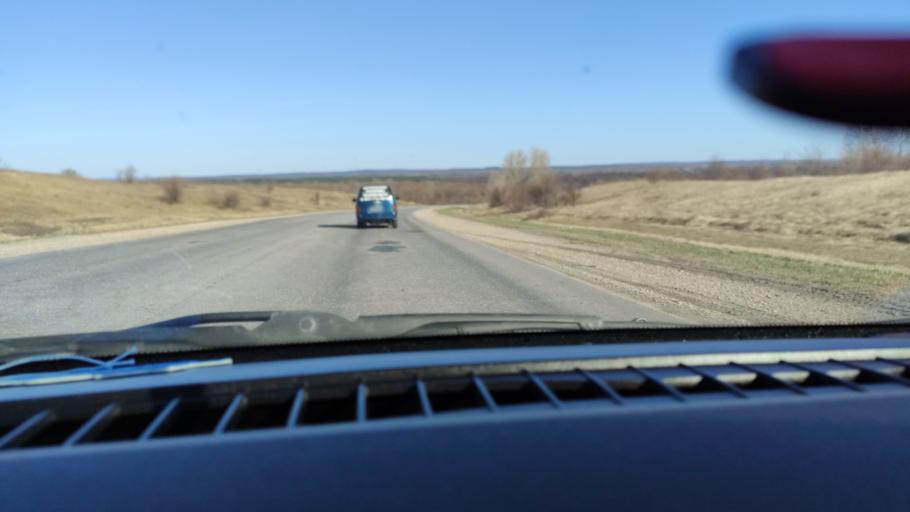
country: RU
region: Samara
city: Varlamovo
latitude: 53.1278
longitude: 48.2894
